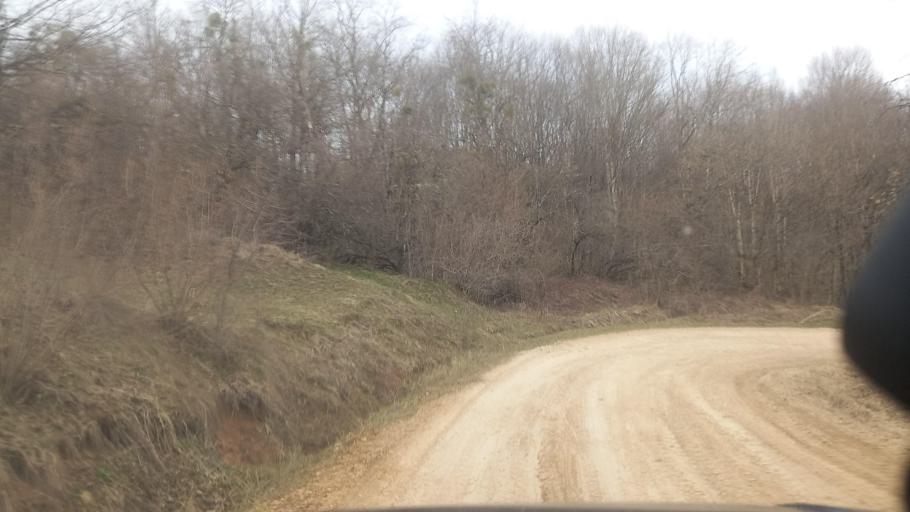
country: RU
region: Adygeya
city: Kamennomostskiy
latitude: 44.2092
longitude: 40.0060
